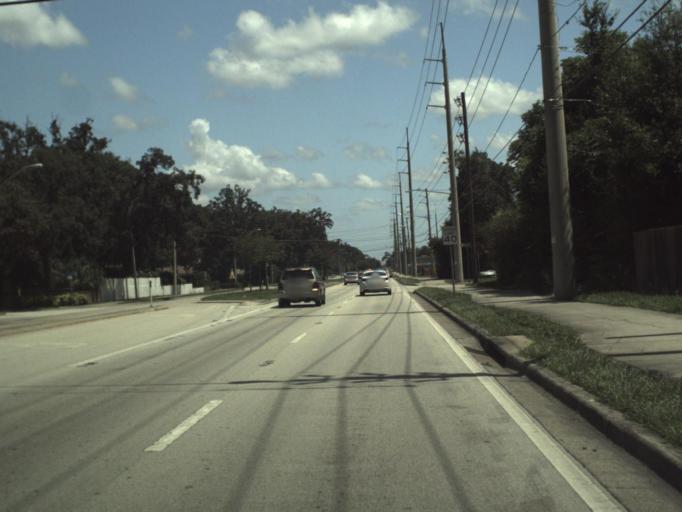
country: US
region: Florida
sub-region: Orange County
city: Conway
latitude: 28.4903
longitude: -81.3307
